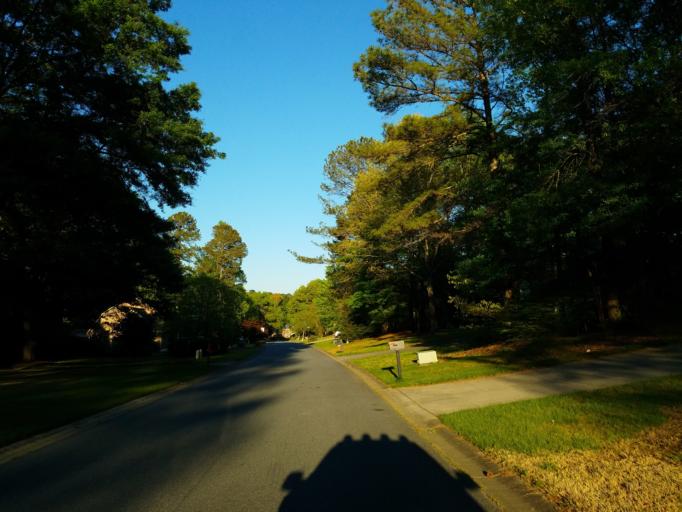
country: US
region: Georgia
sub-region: Cobb County
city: Powder Springs
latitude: 33.9198
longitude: -84.6335
